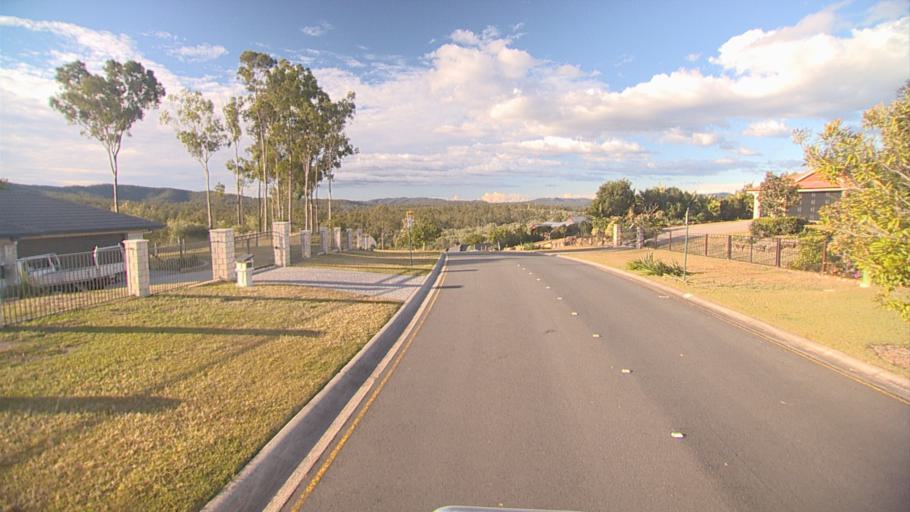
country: AU
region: Queensland
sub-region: Logan
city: Cedar Vale
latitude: -27.8658
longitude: 153.0830
